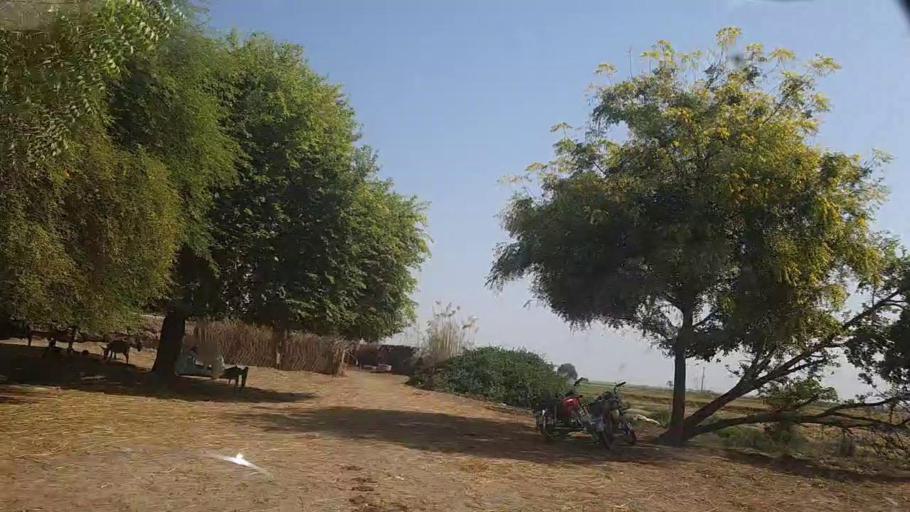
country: PK
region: Sindh
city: Thul
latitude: 28.1117
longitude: 68.7260
